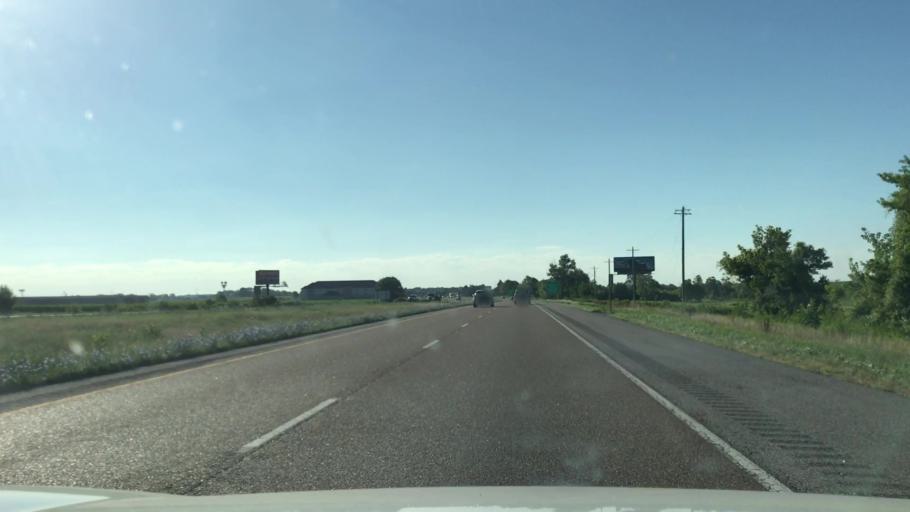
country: US
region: Illinois
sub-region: Saint Clair County
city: Scott Air Force Base
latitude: 38.5560
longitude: -89.8205
